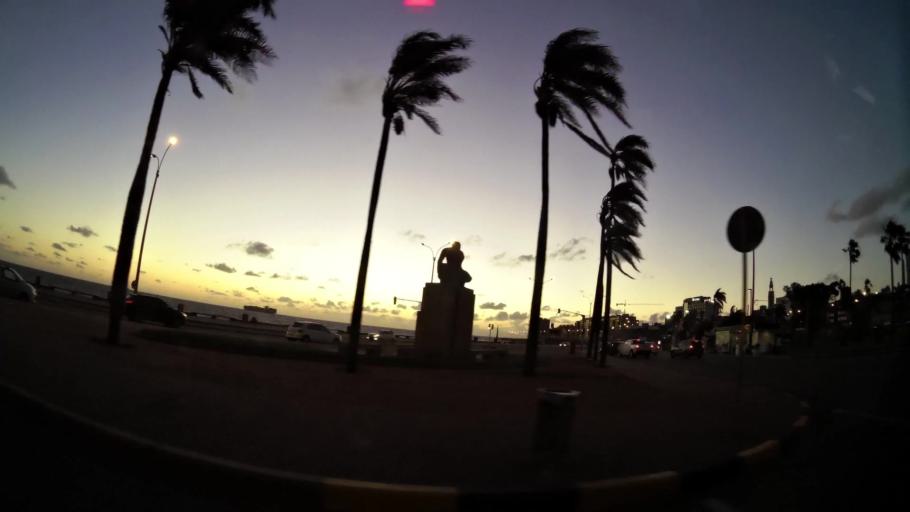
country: UY
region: Montevideo
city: Montevideo
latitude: -34.9104
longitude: -56.2001
